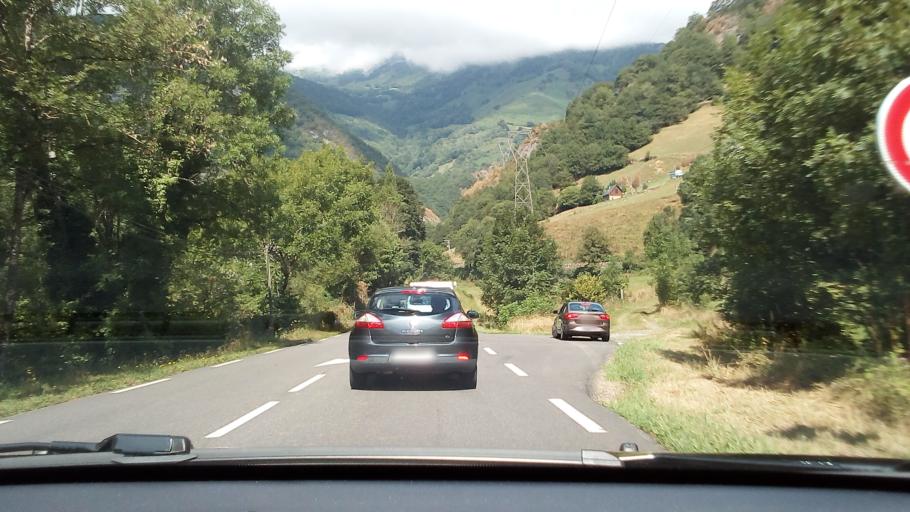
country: FR
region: Aquitaine
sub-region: Departement des Pyrenees-Atlantiques
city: Laruns
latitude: 42.9404
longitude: -0.6018
